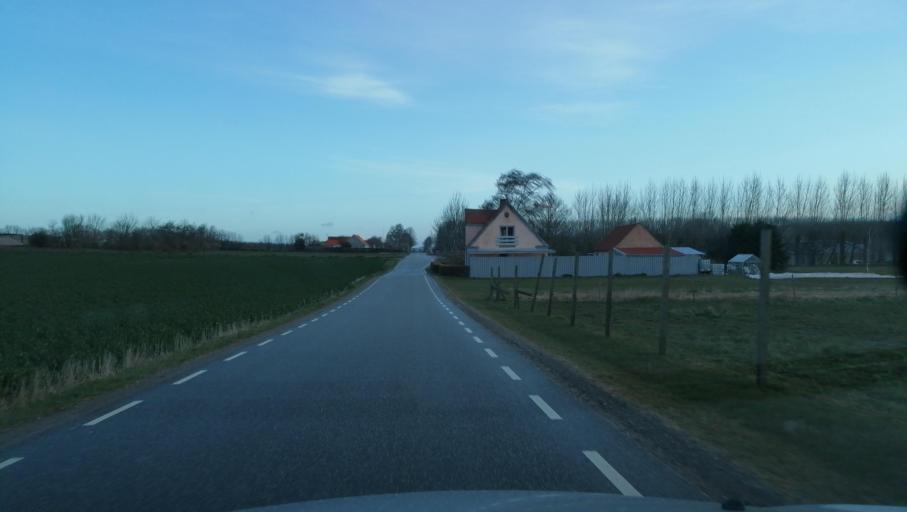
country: DK
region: Zealand
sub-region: Odsherred Kommune
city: Horve
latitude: 55.7563
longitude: 11.4403
